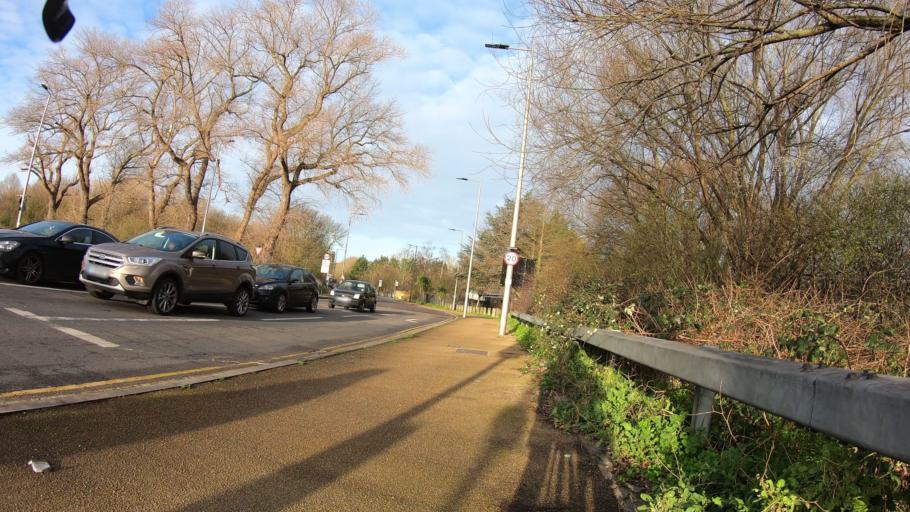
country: GB
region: England
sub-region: Greater London
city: Hackney
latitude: 51.5510
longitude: -0.0195
